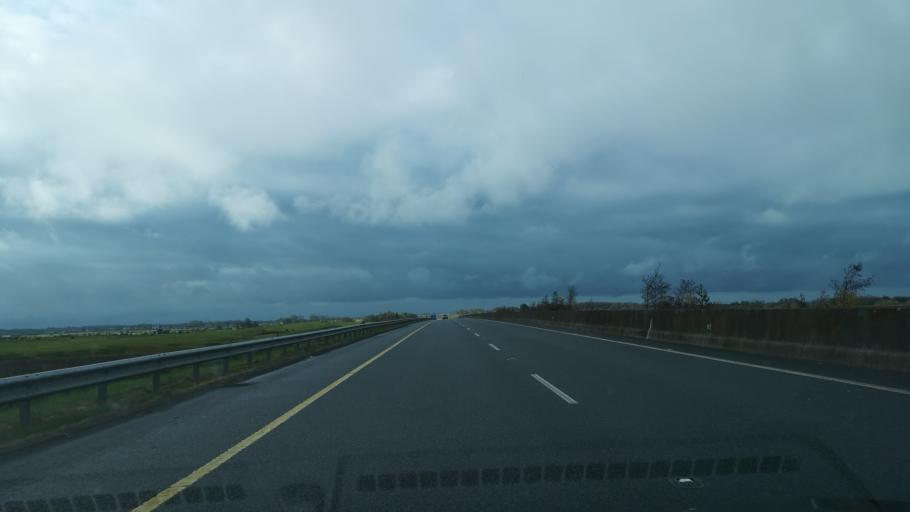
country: IE
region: Connaught
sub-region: County Galway
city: Loughrea
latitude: 53.2746
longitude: -8.5596
